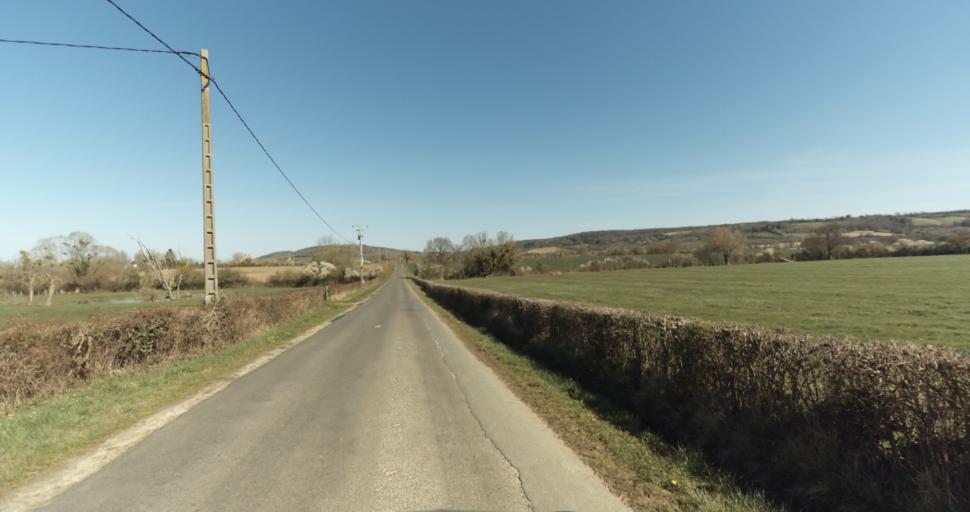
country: FR
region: Lower Normandy
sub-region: Departement du Calvados
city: Saint-Pierre-sur-Dives
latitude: 48.9555
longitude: 0.0495
